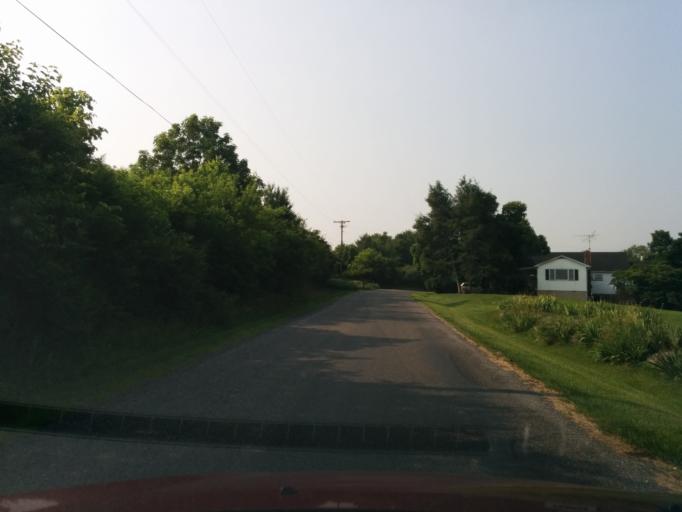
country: US
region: Virginia
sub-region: City of Lexington
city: Lexington
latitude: 37.7694
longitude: -79.4373
